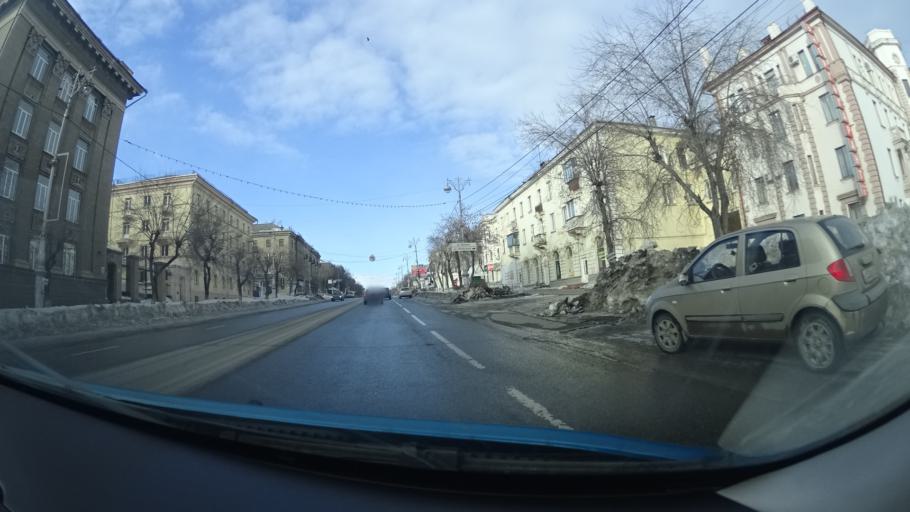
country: RU
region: Chelyabinsk
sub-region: Gorod Magnitogorsk
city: Magnitogorsk
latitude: 53.4273
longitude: 58.9836
